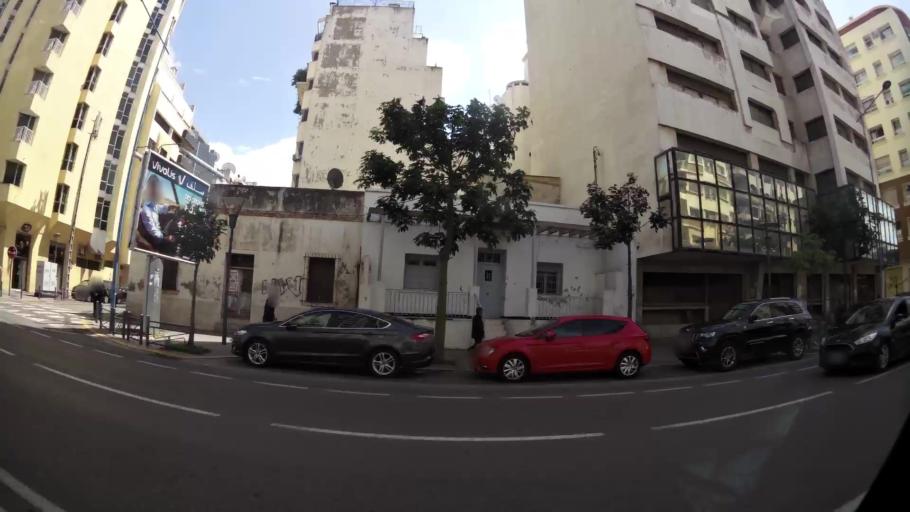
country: MA
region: Grand Casablanca
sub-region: Casablanca
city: Casablanca
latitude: 33.5923
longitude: -7.6384
